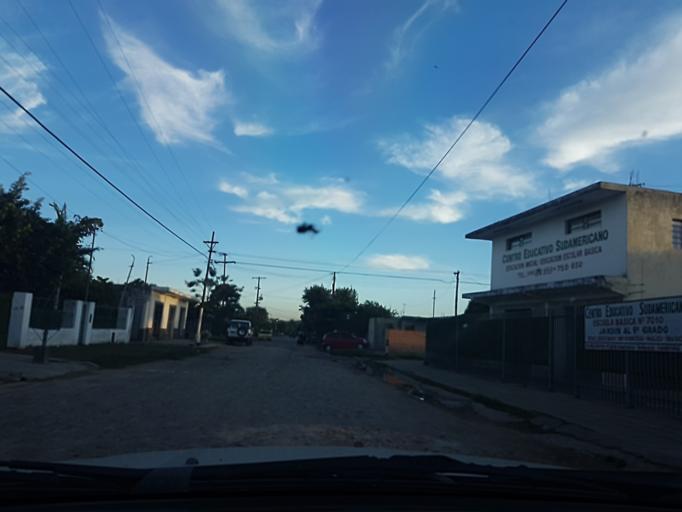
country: PY
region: Central
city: Colonia Mariano Roque Alonso
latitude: -25.2080
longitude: -57.5390
